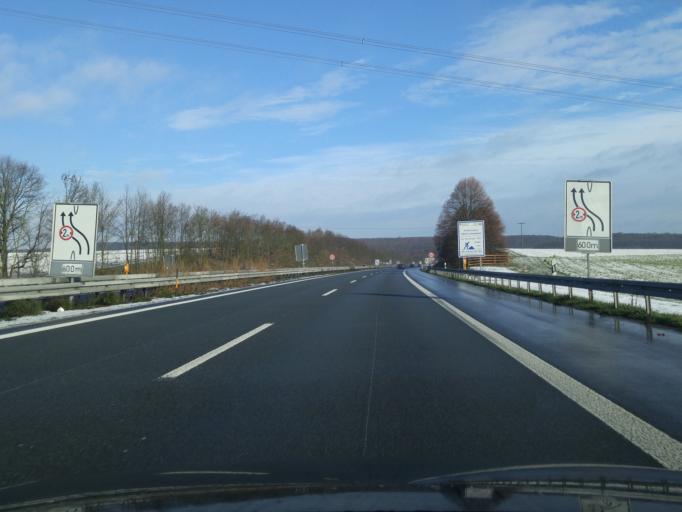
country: DE
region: Bavaria
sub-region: Regierungsbezirk Unterfranken
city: Werneck
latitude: 49.9805
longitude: 10.0428
